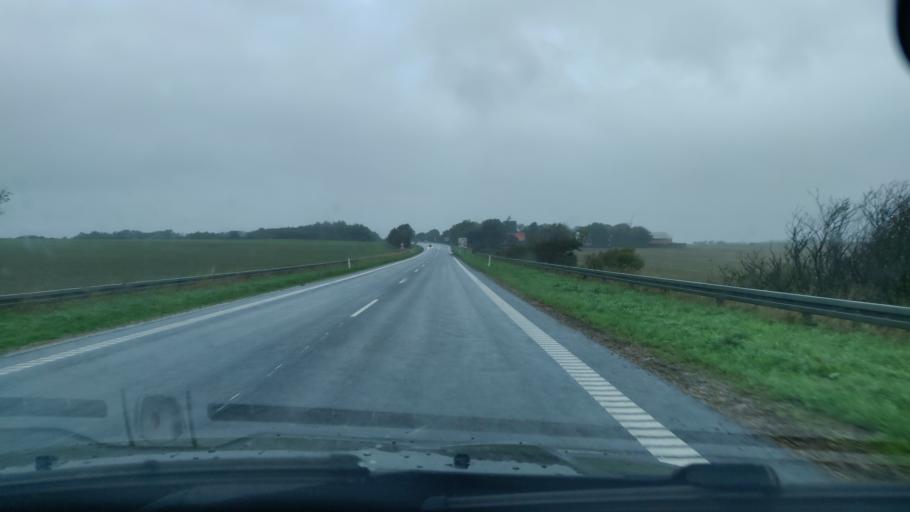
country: DK
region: North Denmark
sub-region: Thisted Kommune
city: Thisted
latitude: 56.8797
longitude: 8.5929
